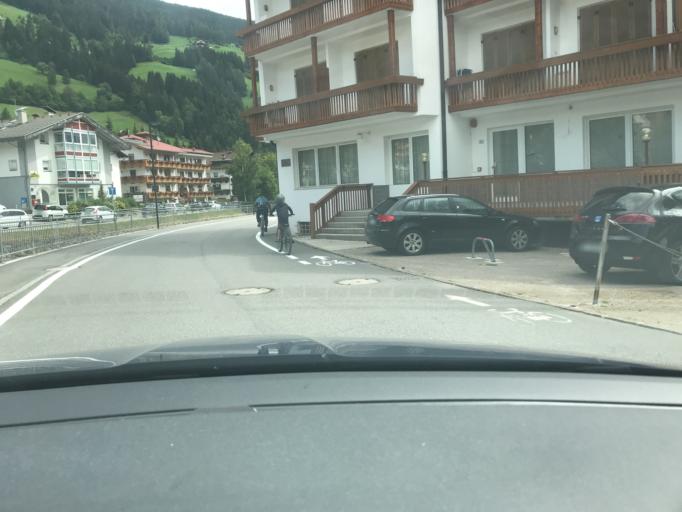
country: IT
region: Trentino-Alto Adige
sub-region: Bolzano
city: San Candido
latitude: 46.7339
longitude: 12.2789
